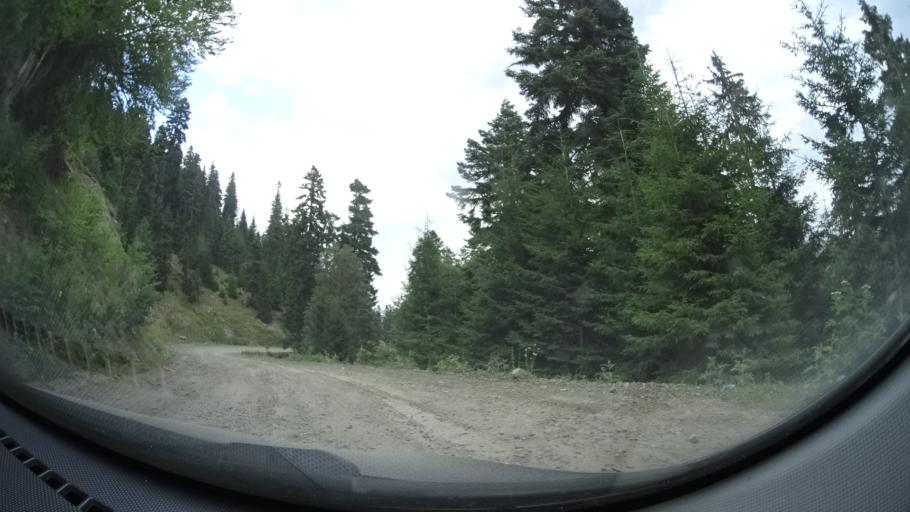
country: GE
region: Samtskhe-Javakheti
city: Adigeni
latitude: 41.6313
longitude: 42.5738
